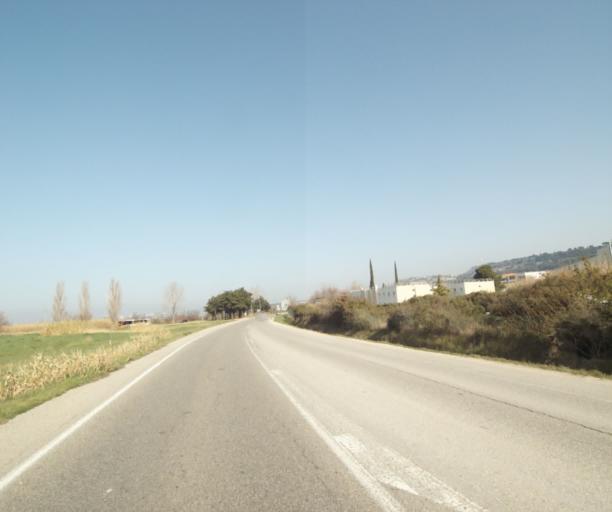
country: FR
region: Provence-Alpes-Cote d'Azur
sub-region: Departement des Bouches-du-Rhone
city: Vitrolles
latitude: 43.4464
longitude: 5.2305
